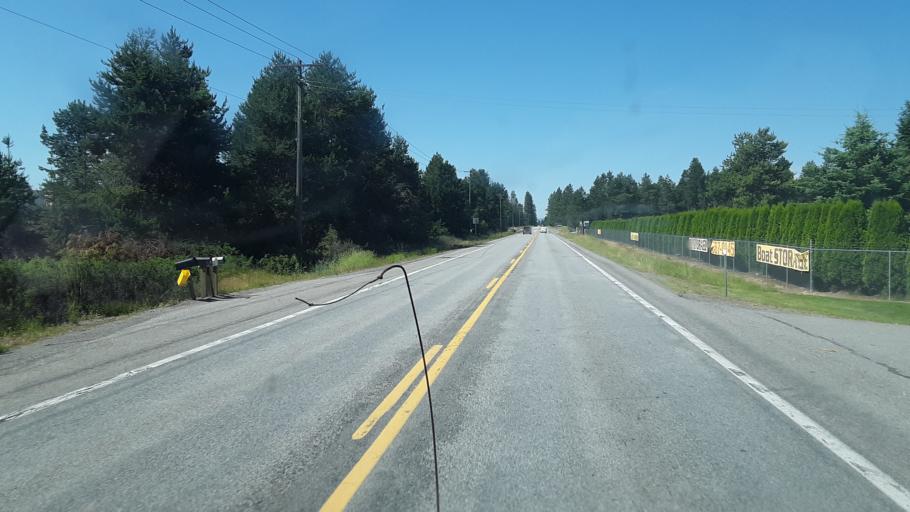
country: US
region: Idaho
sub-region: Kootenai County
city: Post Falls
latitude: 47.7791
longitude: -116.9542
